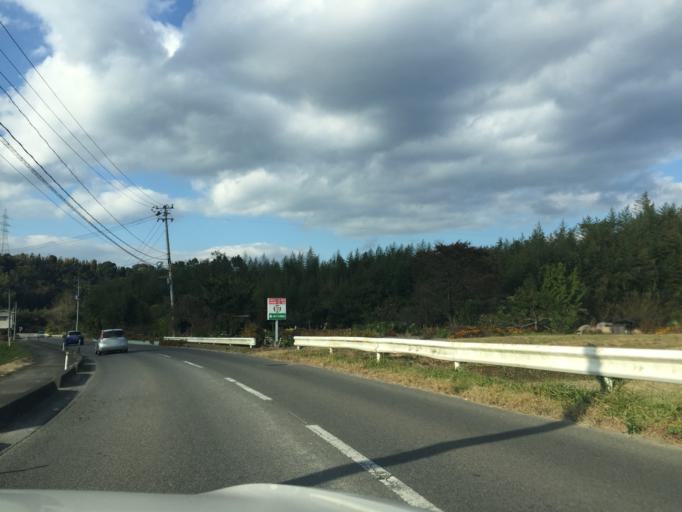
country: JP
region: Fukushima
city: Iwaki
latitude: 37.1133
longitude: 140.8619
